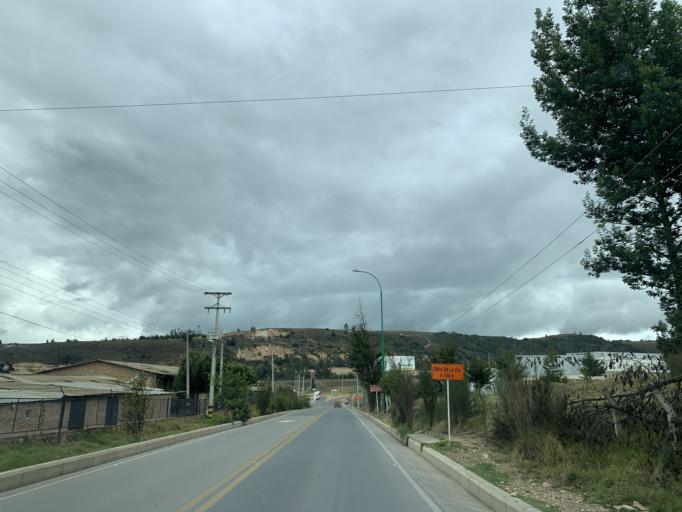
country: CO
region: Boyaca
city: Tunja
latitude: 5.5342
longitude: -73.3450
